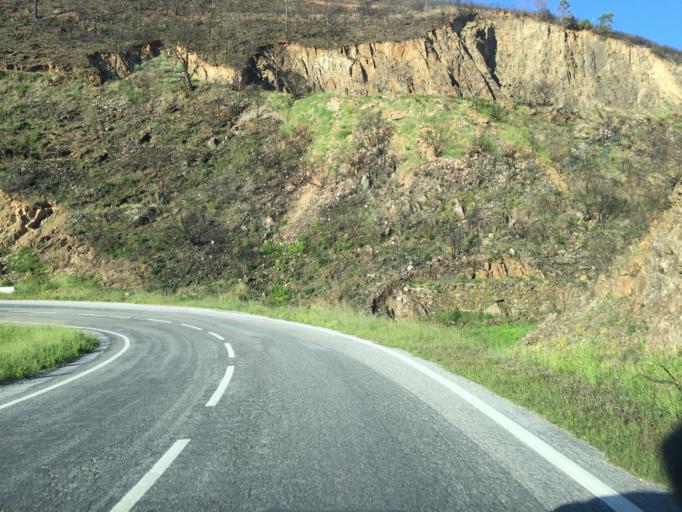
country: PT
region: Coimbra
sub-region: Pampilhosa da Serra
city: Pampilhosa da Serra
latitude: 40.0295
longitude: -7.9606
